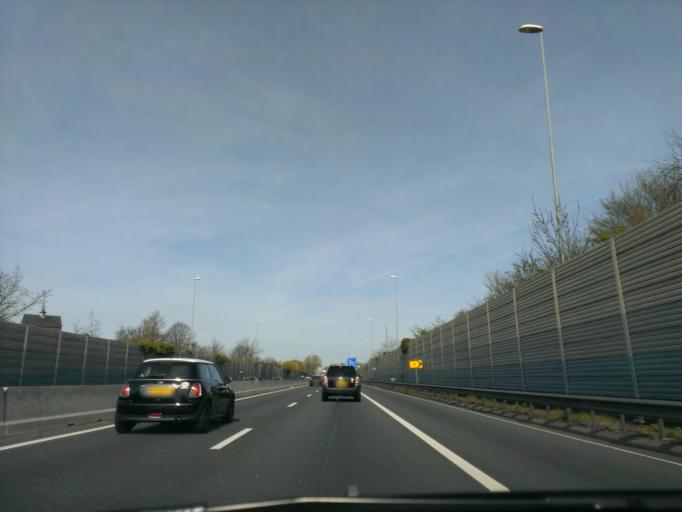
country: NL
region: North Holland
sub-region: Gemeente Aalsmeer
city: Aalsmeer
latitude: 52.3355
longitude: 4.7825
